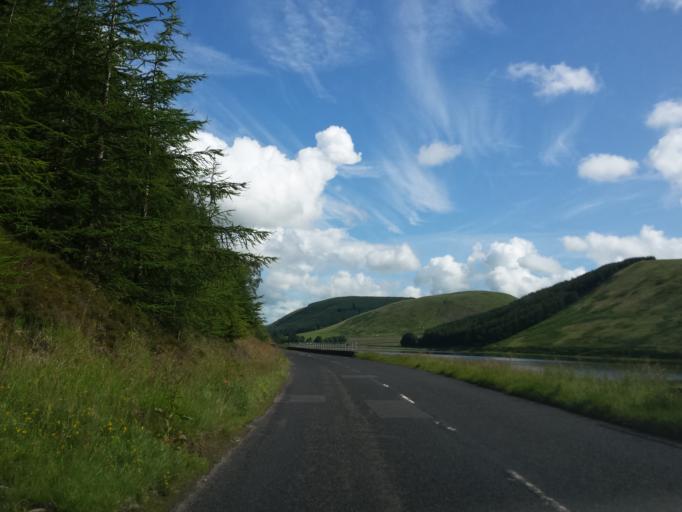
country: GB
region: Scotland
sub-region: The Scottish Borders
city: Peebles
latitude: 55.4620
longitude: -3.2132
